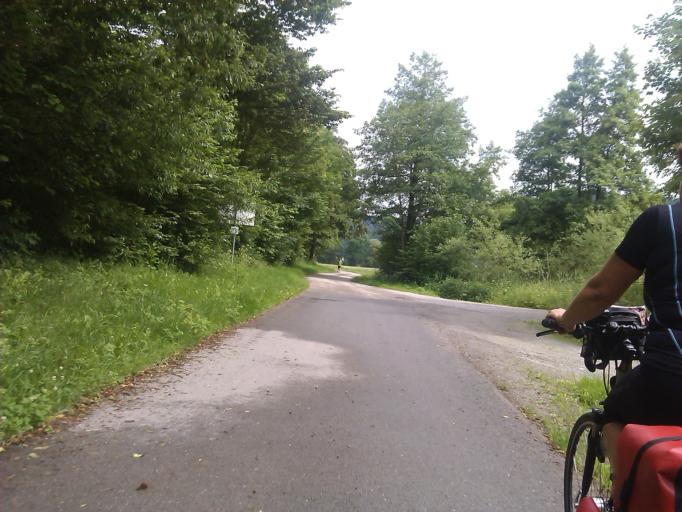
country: DE
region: Baden-Wuerttemberg
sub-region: Regierungsbezirk Stuttgart
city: Gaildorf
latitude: 48.9708
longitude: 9.8169
